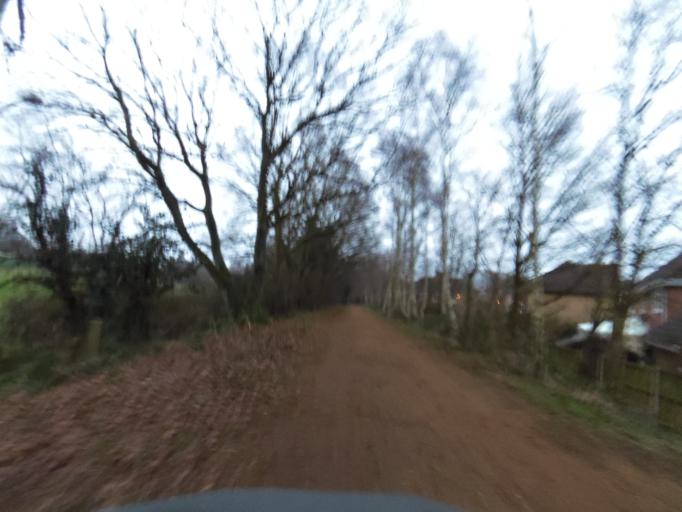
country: GB
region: England
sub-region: Norfolk
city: Costessey
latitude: 52.6839
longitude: 1.2143
